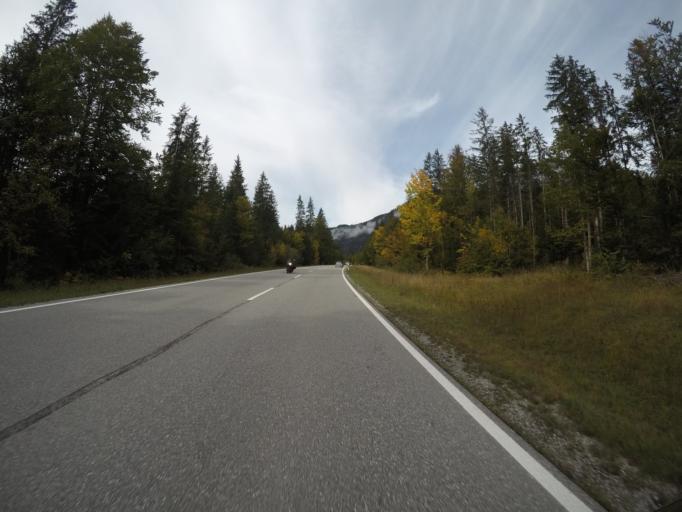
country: DE
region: Bavaria
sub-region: Upper Bavaria
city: Jachenau
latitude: 47.5586
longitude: 11.4755
